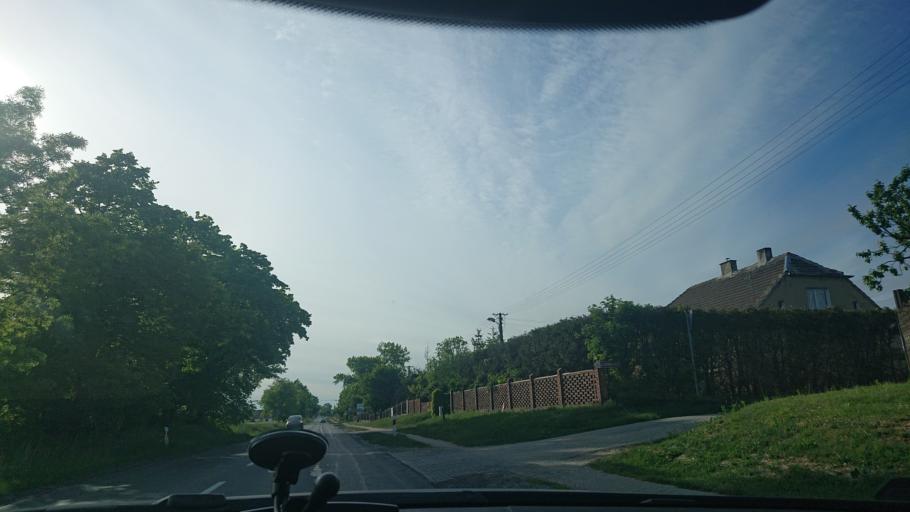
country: PL
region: Greater Poland Voivodeship
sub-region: Powiat gnieznienski
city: Gniezno
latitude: 52.5459
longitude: 17.5646
